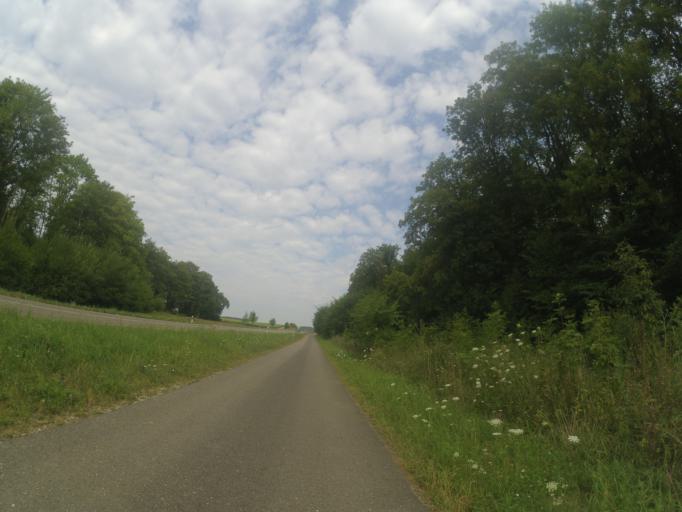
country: DE
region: Baden-Wuerttemberg
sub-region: Tuebingen Region
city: Lonsee
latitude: 48.5113
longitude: 9.9163
